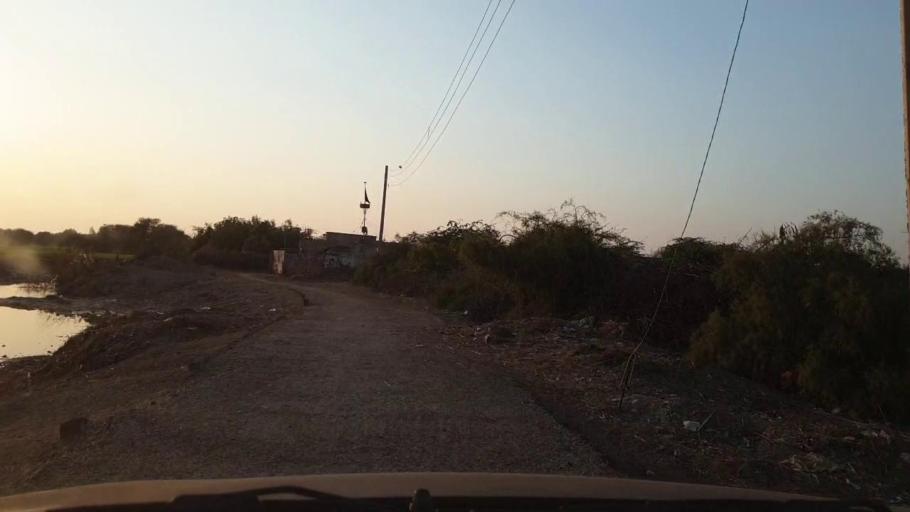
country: PK
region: Sindh
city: Jhol
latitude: 25.9251
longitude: 68.9420
